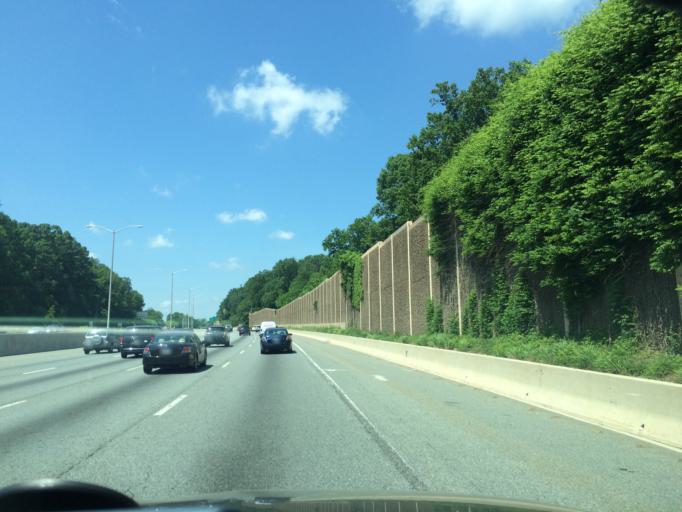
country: US
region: Maryland
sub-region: Baltimore County
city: Pikesville
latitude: 39.3949
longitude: -76.7006
